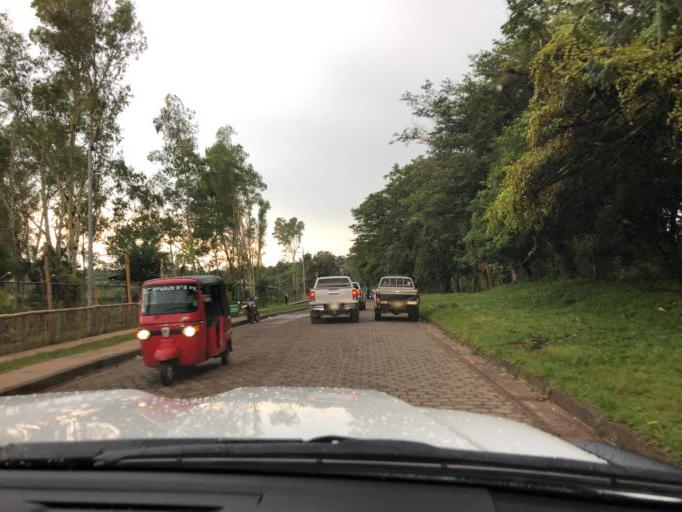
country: NI
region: Chontales
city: La Libertad
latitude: 12.2114
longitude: -85.1681
